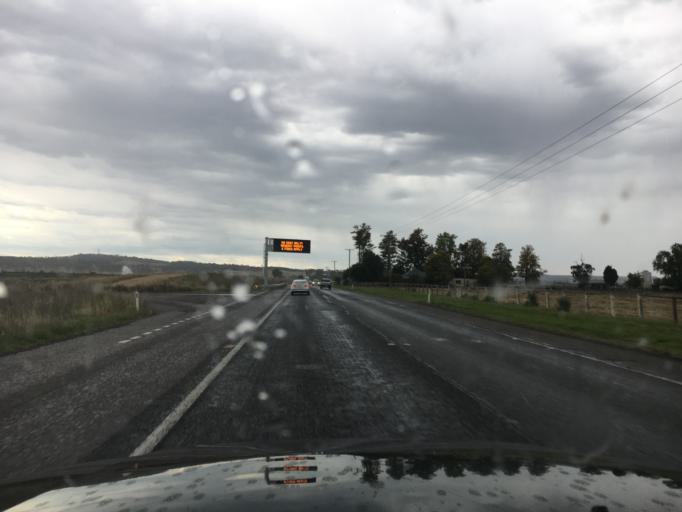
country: AU
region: New South Wales
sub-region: Muswellbrook
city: Muswellbrook
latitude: -32.2207
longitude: 150.9003
